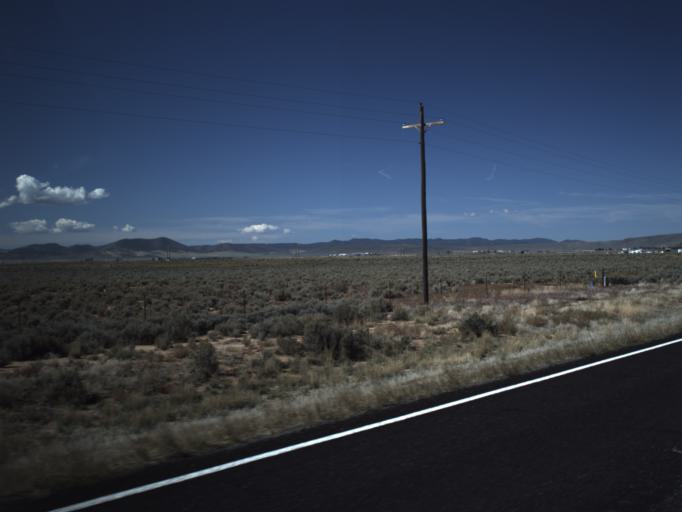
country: US
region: Utah
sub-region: Washington County
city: Enterprise
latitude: 37.6876
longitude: -113.5952
